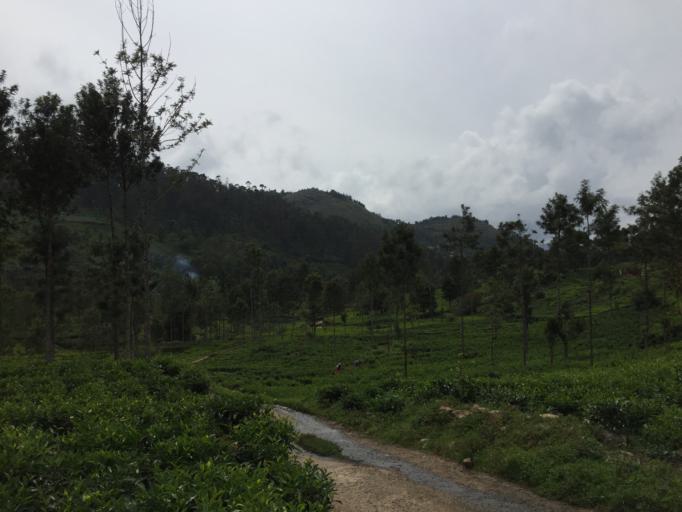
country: IN
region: Tamil Nadu
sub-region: Nilgiri
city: Kotagiri
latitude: 11.4594
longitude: 76.8598
